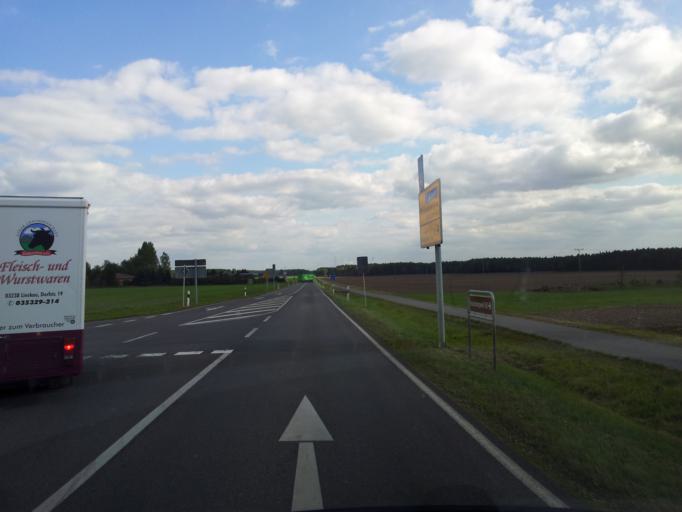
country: DE
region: Brandenburg
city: Sallgast
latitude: 51.6184
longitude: 13.8148
